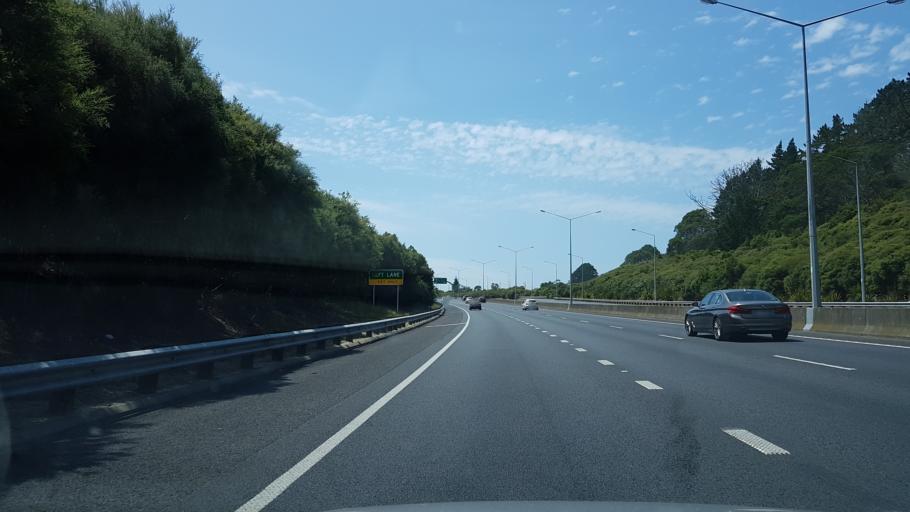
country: NZ
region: Auckland
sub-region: Auckland
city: Rothesay Bay
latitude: -36.7624
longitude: 174.6988
